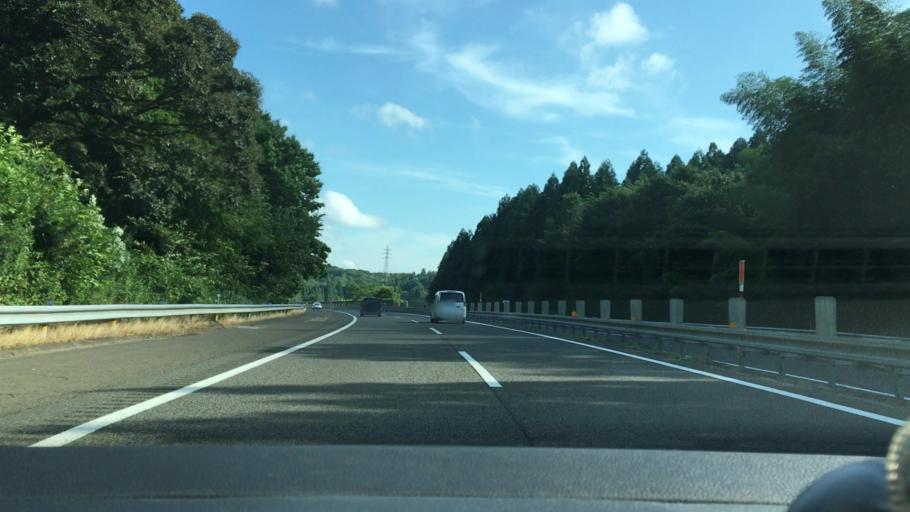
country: JP
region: Fukui
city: Maruoka
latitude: 36.2573
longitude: 136.2826
